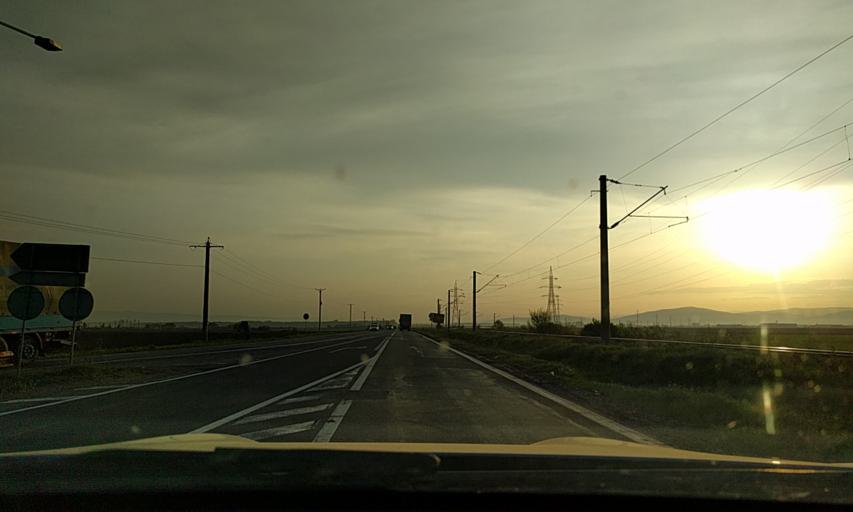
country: RO
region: Brasov
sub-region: Comuna Harman
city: Harman
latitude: 45.7126
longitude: 25.7095
